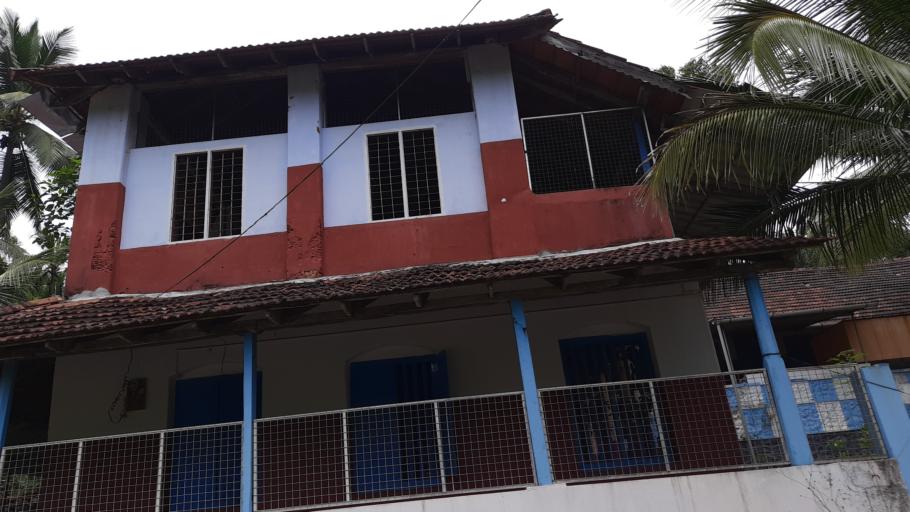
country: IN
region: Kerala
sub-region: Kottayam
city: Lalam
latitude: 9.8227
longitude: 76.7241
